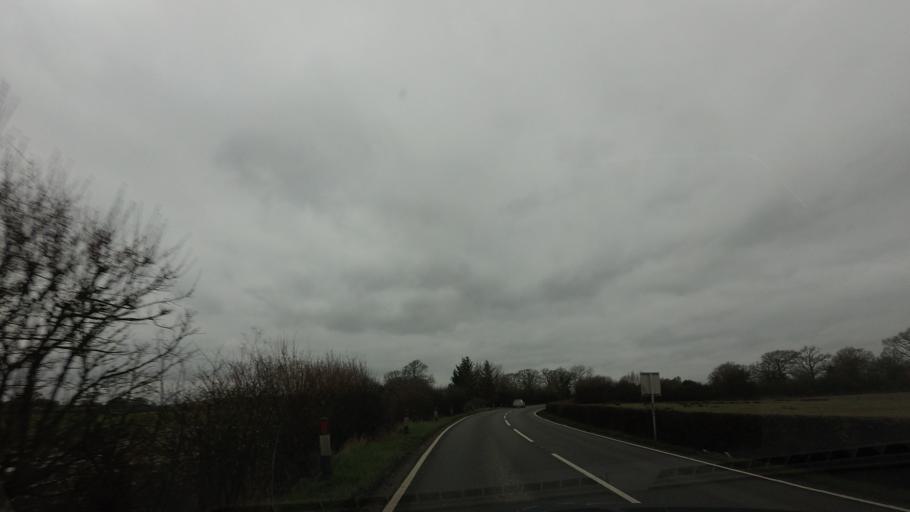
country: GB
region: England
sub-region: Kent
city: Staplehurst
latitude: 51.1924
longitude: 0.5357
